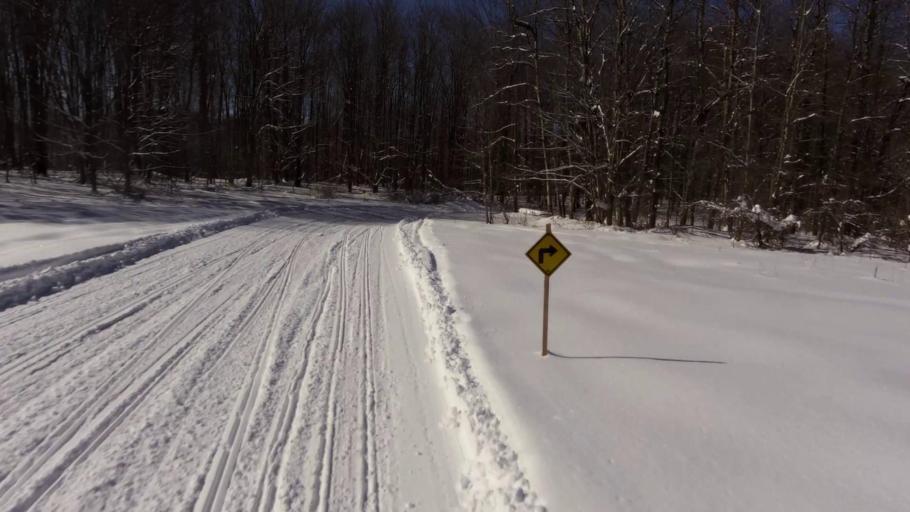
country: US
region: New York
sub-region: Chautauqua County
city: Mayville
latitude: 42.2234
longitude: -79.4012
